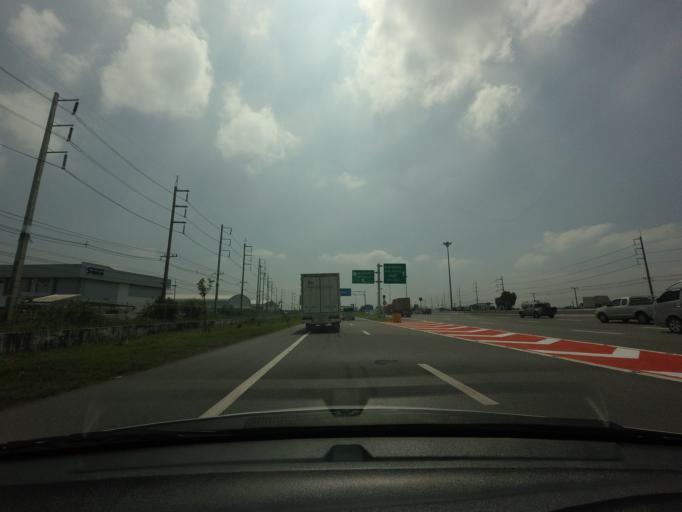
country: TH
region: Chachoengsao
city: Bang Pakong
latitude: 13.5631
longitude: 100.9892
